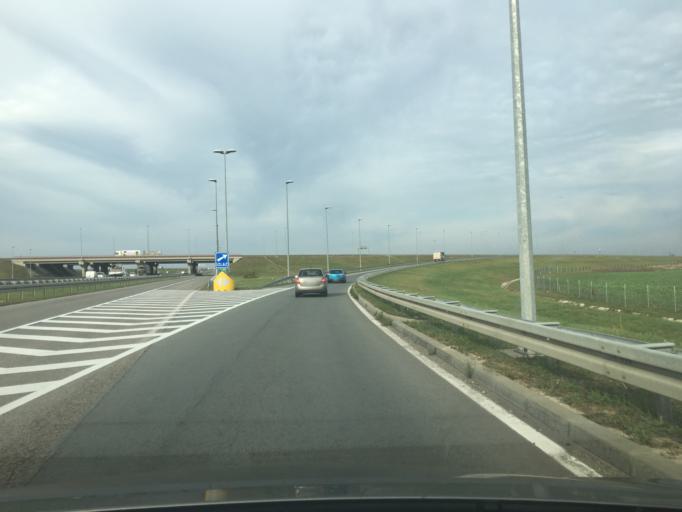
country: RS
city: Dobanovci
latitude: 44.8359
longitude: 20.2539
